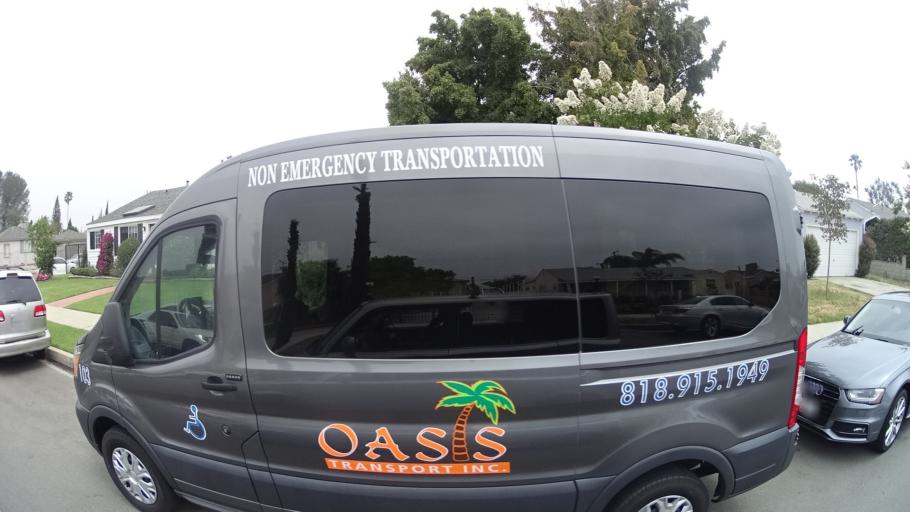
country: US
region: California
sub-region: Los Angeles County
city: North Hollywood
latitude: 34.1875
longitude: -118.4077
